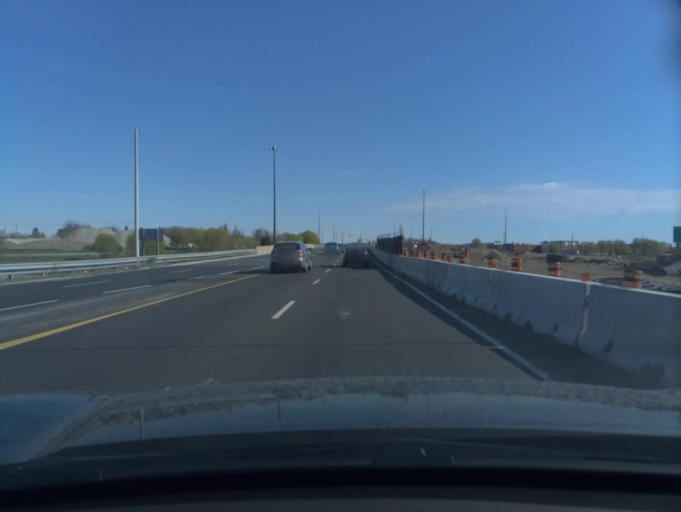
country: CA
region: Ontario
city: North Perth
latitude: 43.8263
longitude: -80.9999
